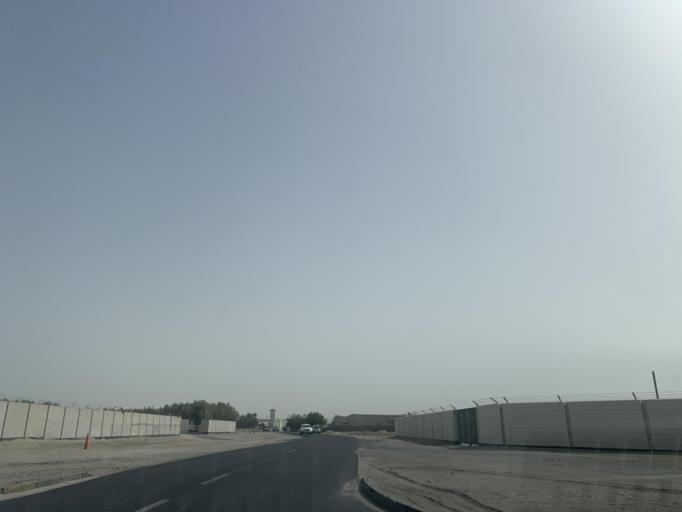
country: BH
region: Northern
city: Sitrah
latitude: 26.1759
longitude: 50.6211
